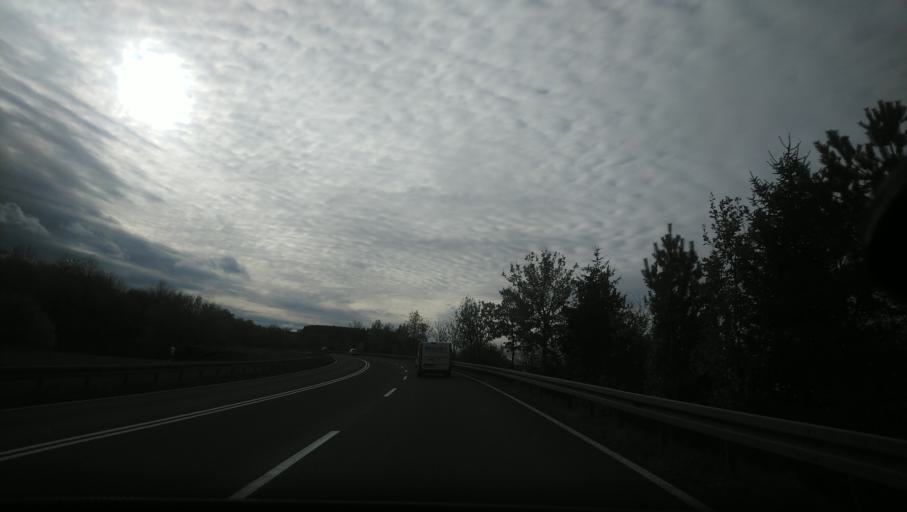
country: DE
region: Saxony
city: Zwonitz
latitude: 50.6352
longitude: 12.8198
